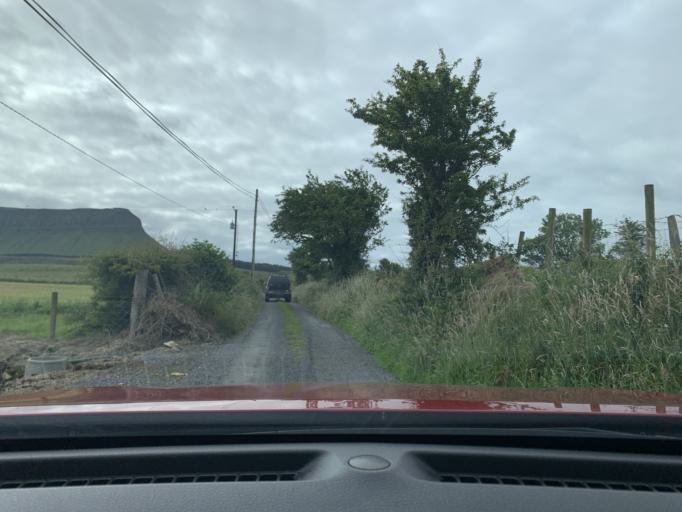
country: IE
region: Connaught
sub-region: Sligo
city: Sligo
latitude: 54.3778
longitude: -8.5205
